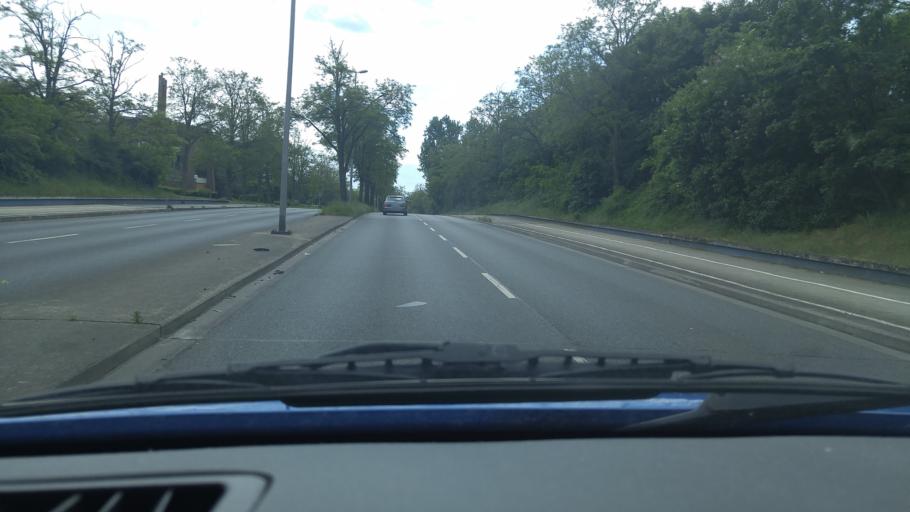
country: DE
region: Hesse
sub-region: Regierungsbezirk Darmstadt
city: Russelsheim
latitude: 49.9936
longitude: 8.4246
